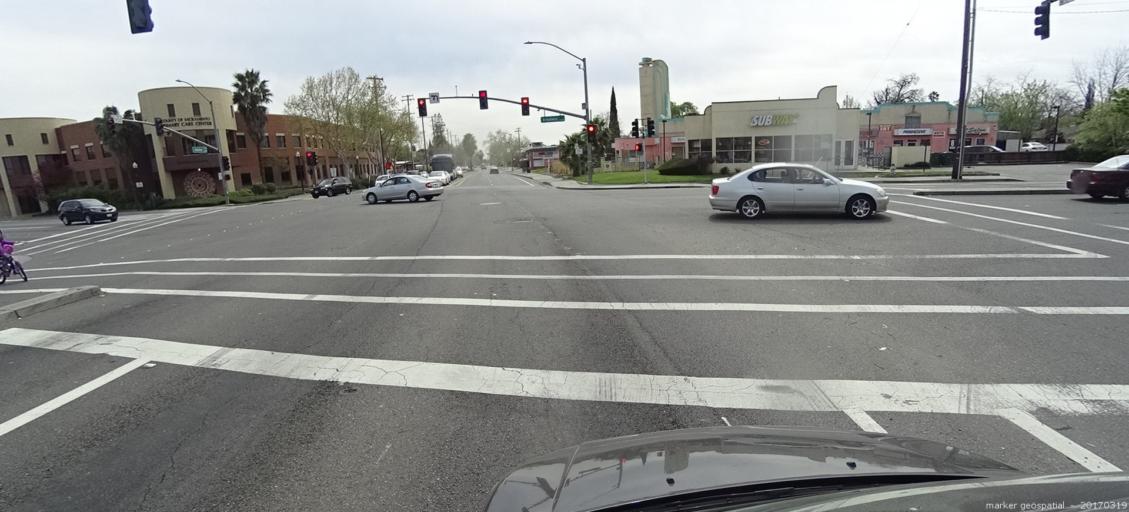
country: US
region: California
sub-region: Sacramento County
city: Parkway
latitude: 38.5470
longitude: -121.4540
